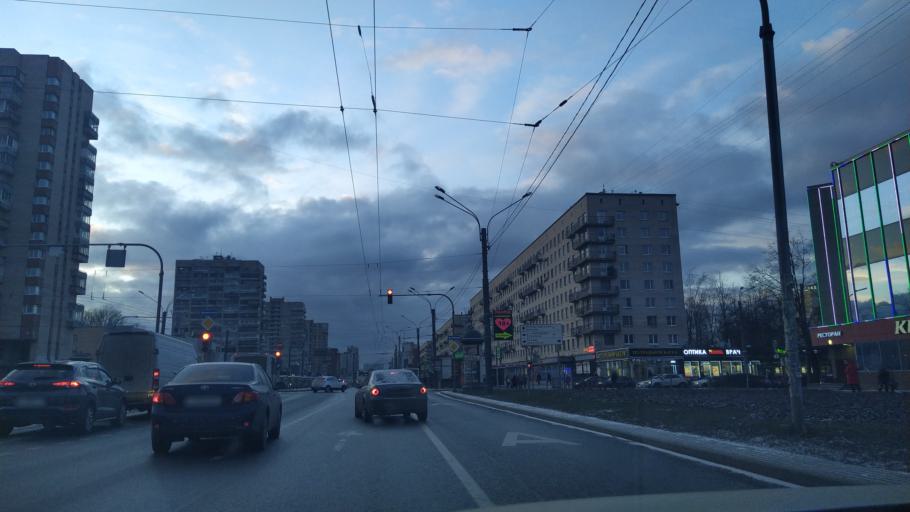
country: RU
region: St.-Petersburg
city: Dachnoye
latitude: 59.8520
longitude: 30.2688
